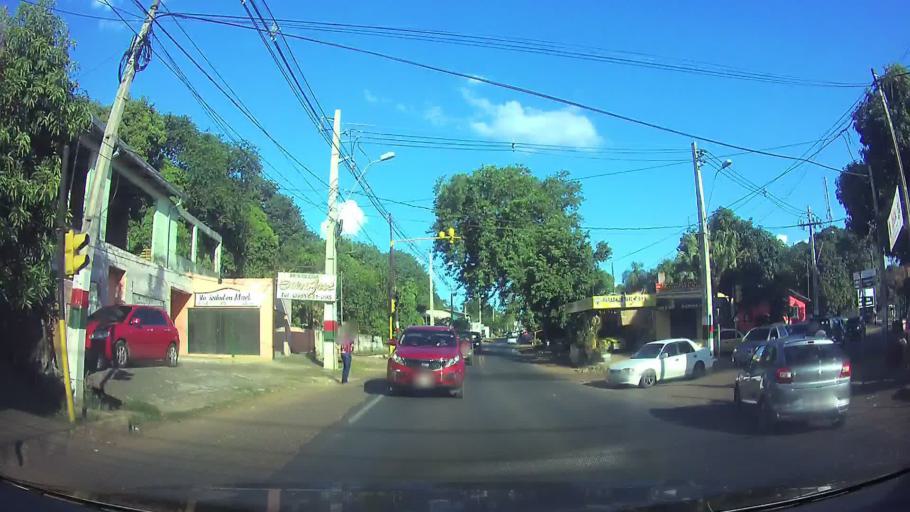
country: PY
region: Central
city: Aregua
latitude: -25.2928
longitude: -57.4412
